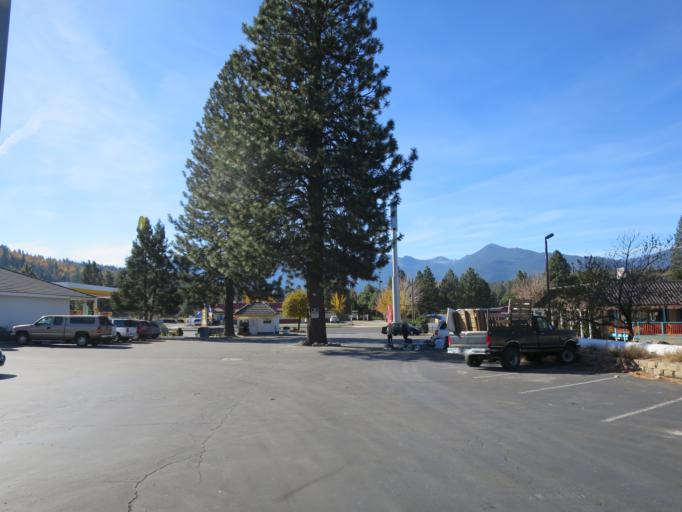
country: US
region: California
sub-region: Siskiyou County
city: Weed
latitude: 41.3985
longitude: -122.3786
